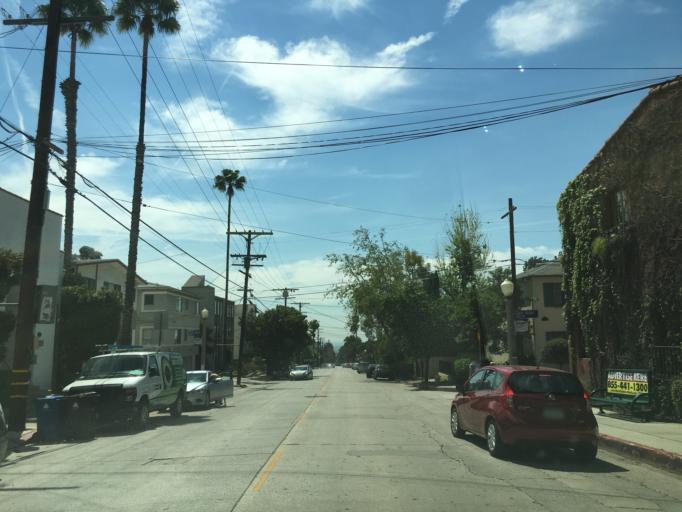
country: US
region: California
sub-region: Los Angeles County
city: Hollywood
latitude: 34.1175
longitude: -118.3215
